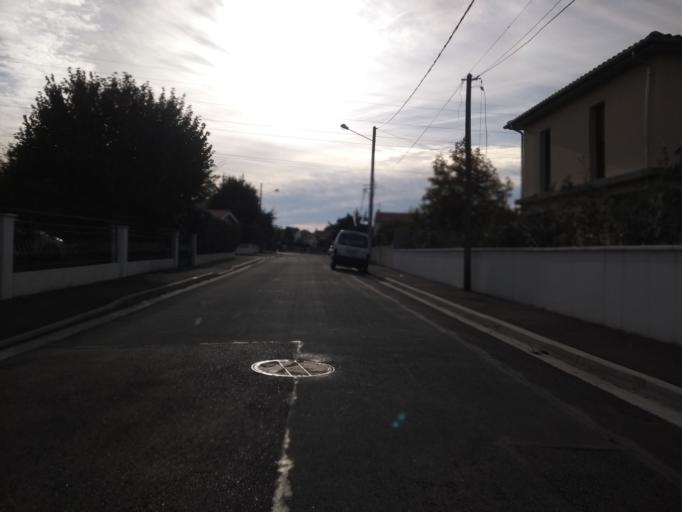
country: FR
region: Aquitaine
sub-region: Departement de la Gironde
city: Pessac
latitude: 44.7906
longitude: -0.6699
